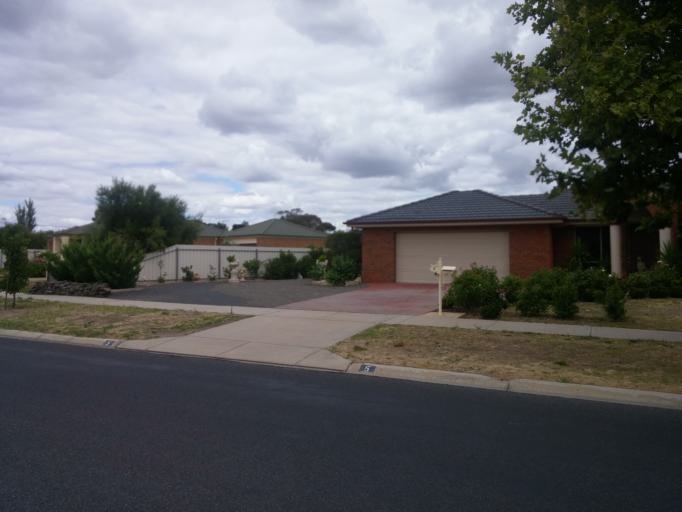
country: AU
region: Victoria
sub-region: Horsham
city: Horsham
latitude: -36.7263
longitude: 142.2014
